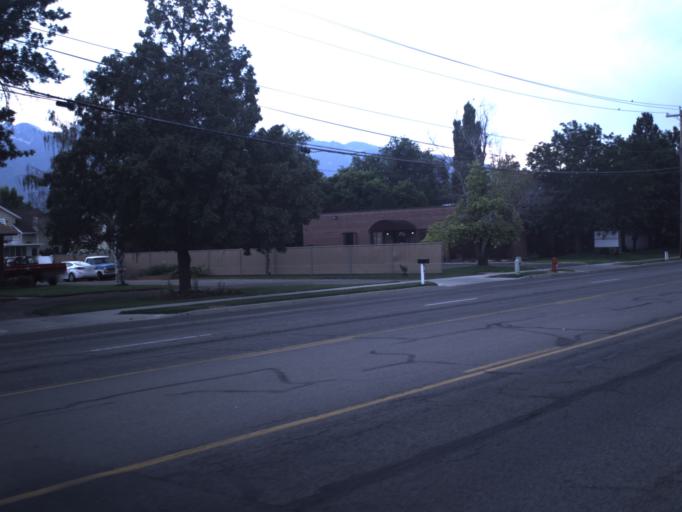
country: US
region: Utah
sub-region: Salt Lake County
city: Sandy City
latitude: 40.6027
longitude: -111.8723
